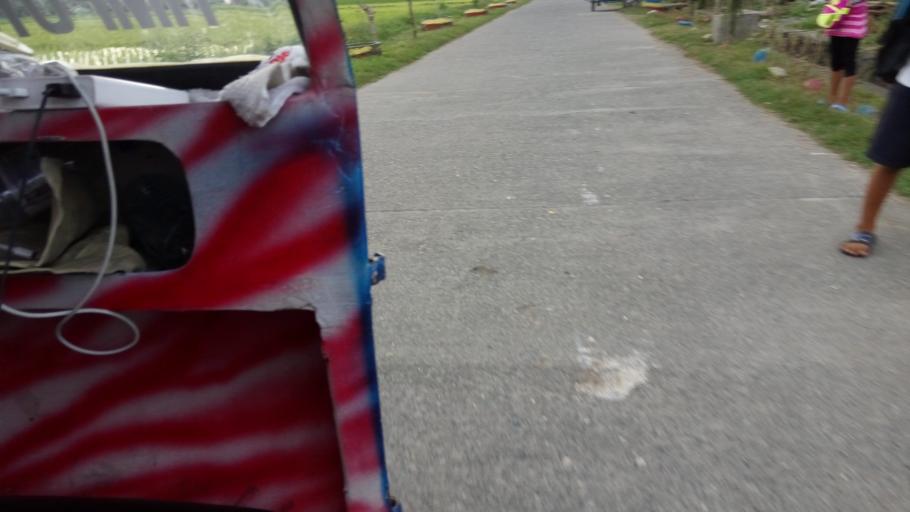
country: PH
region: Ilocos
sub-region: Province of La Union
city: Namboongan
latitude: 16.2937
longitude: 120.3818
